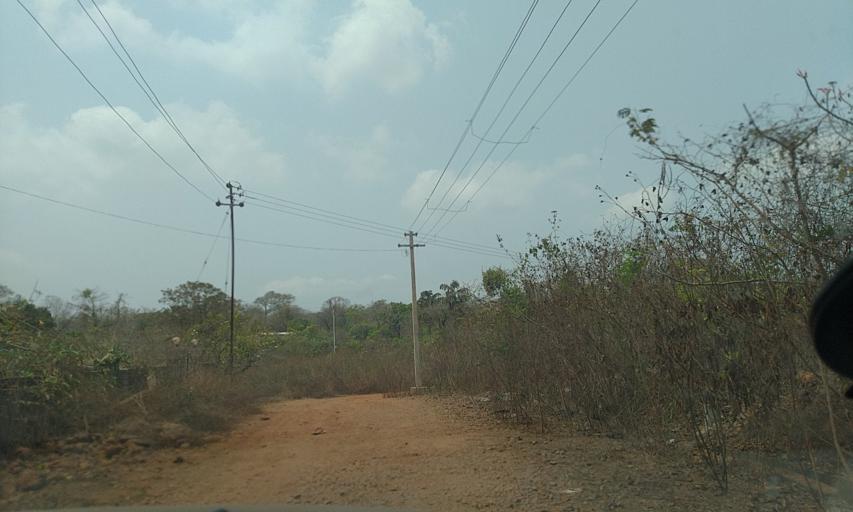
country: IN
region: Goa
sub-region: North Goa
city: Goa Velha
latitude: 15.4843
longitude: 73.9132
